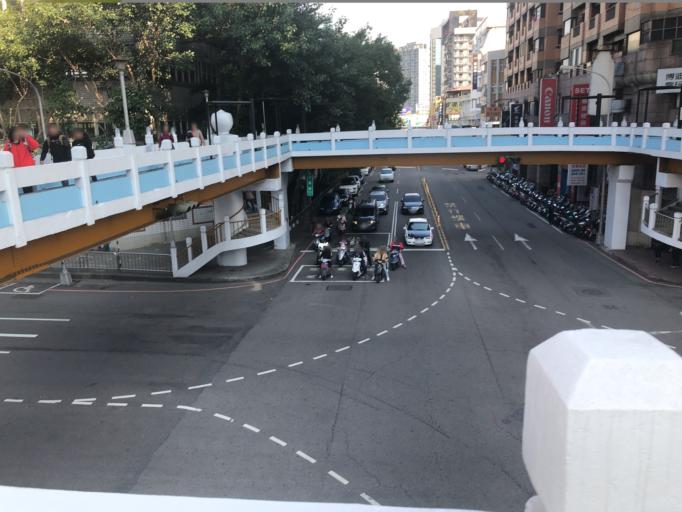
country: TW
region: Taiwan
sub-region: Taichung City
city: Taichung
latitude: 24.1507
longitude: 120.6654
